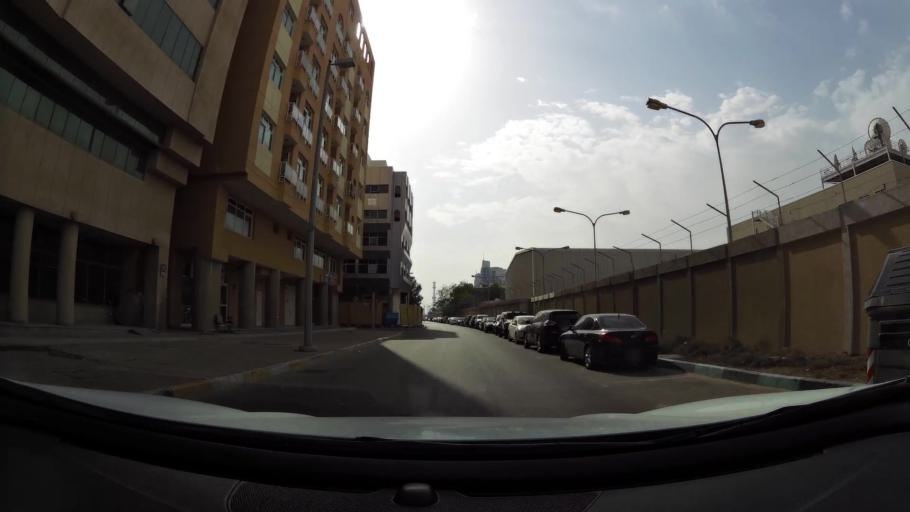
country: AE
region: Abu Dhabi
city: Abu Dhabi
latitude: 24.4581
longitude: 54.3887
